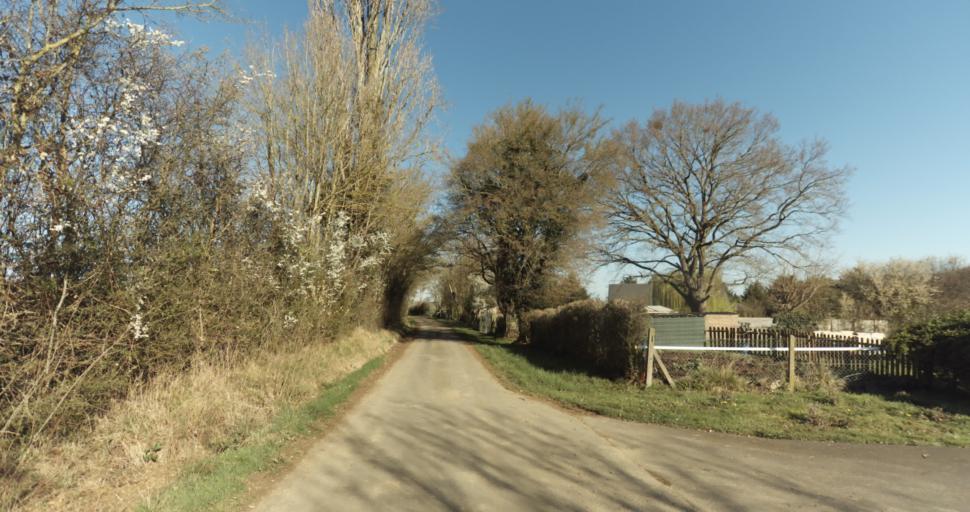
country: FR
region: Lower Normandy
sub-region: Departement du Calvados
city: Saint-Pierre-sur-Dives
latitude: 48.9779
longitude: 0.0342
